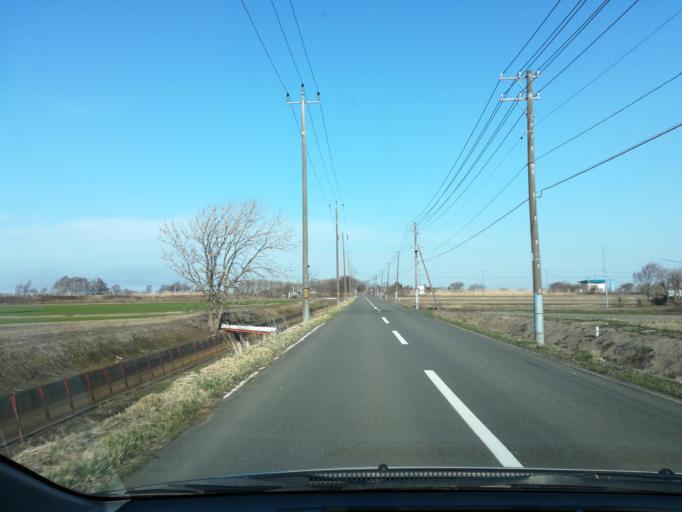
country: JP
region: Hokkaido
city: Ebetsu
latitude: 43.1548
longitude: 141.6441
